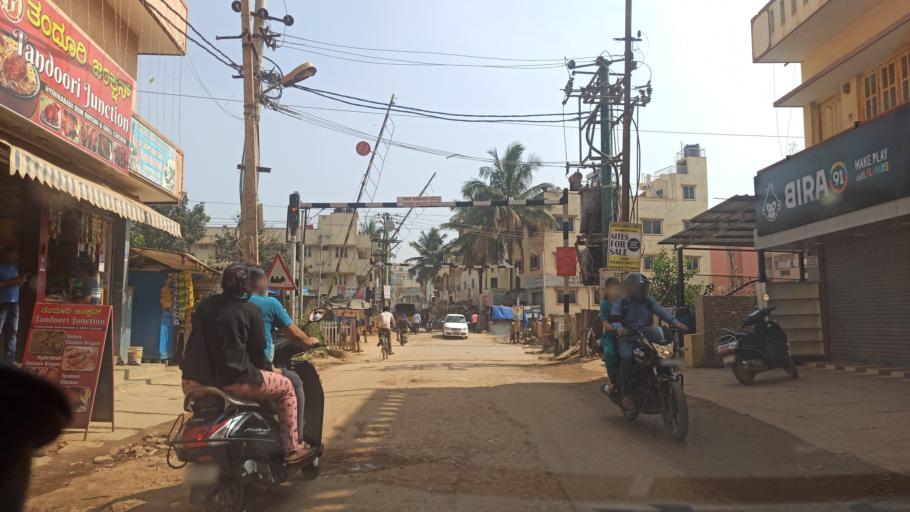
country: IN
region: Karnataka
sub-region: Bangalore Urban
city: Bangalore
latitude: 12.9481
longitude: 77.7054
